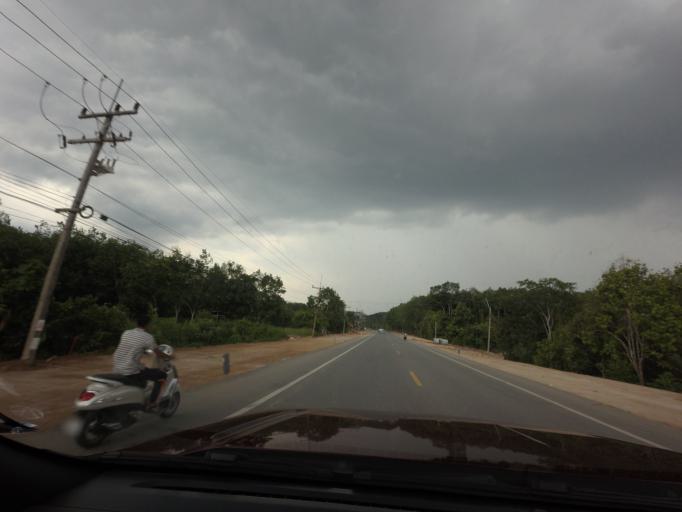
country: TH
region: Yala
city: Krong Pi Nang
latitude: 6.4097
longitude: 101.2801
